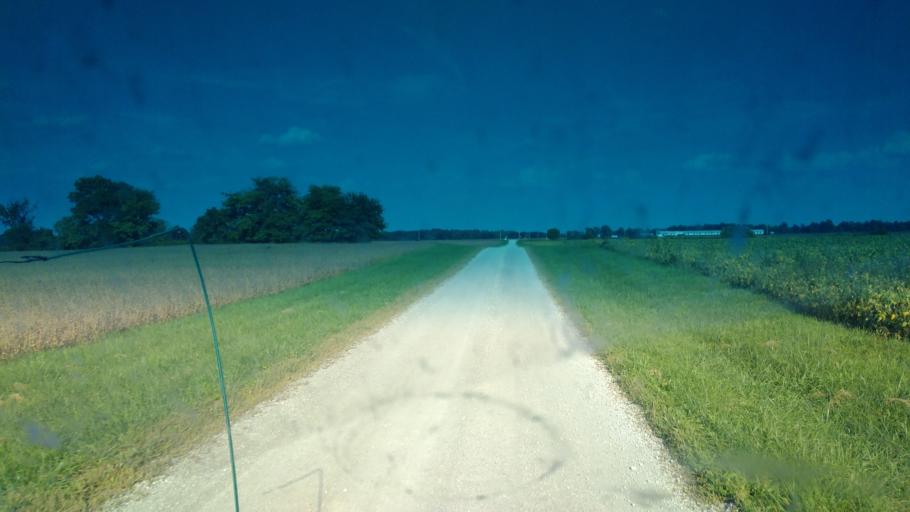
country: US
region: Ohio
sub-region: Wyandot County
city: Upper Sandusky
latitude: 40.9295
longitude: -83.2786
